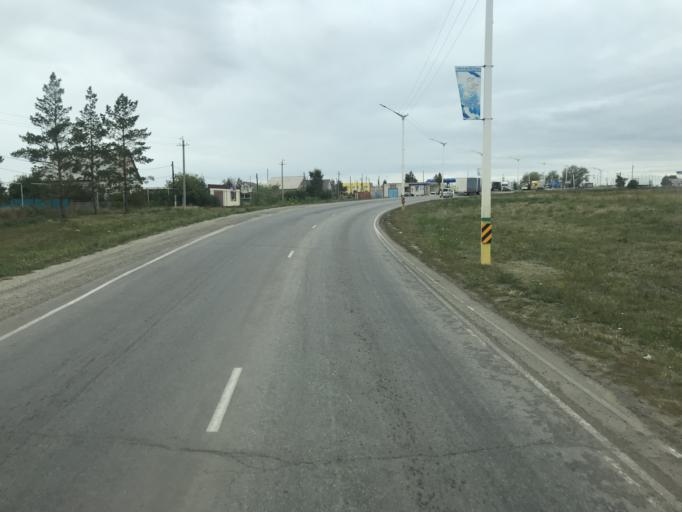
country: KZ
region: Qostanay
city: Komsomolets
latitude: 53.7613
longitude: 62.0752
